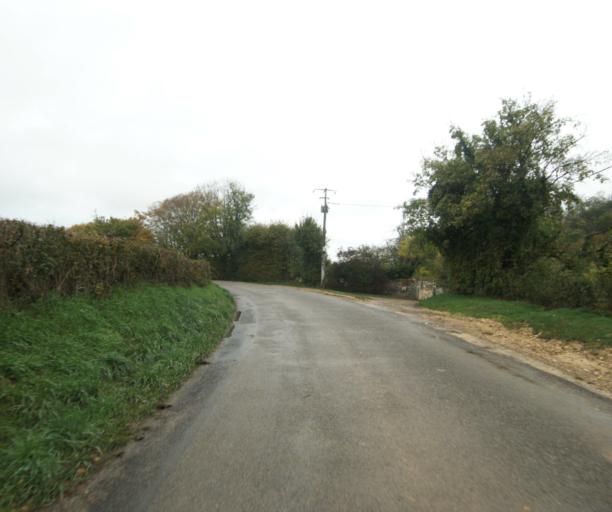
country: FR
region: Bourgogne
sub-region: Departement de Saone-et-Loire
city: Saint-Martin-Belle-Roche
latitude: 46.4763
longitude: 4.8475
